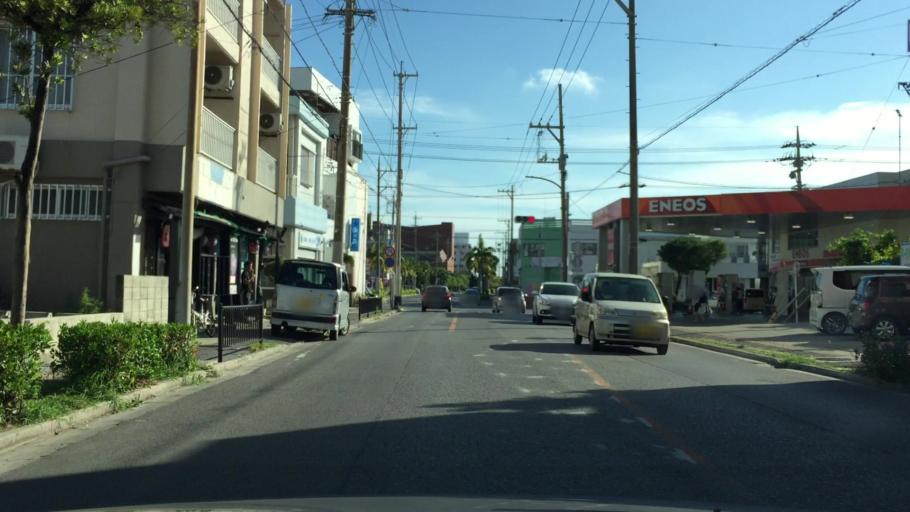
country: JP
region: Okinawa
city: Ishigaki
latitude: 24.3431
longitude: 124.1547
